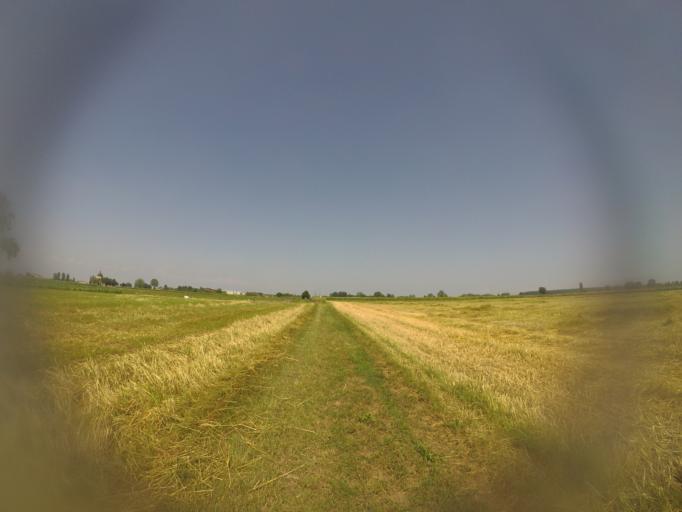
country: IT
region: Friuli Venezia Giulia
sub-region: Provincia di Udine
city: Bertiolo
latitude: 45.9379
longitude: 13.0314
